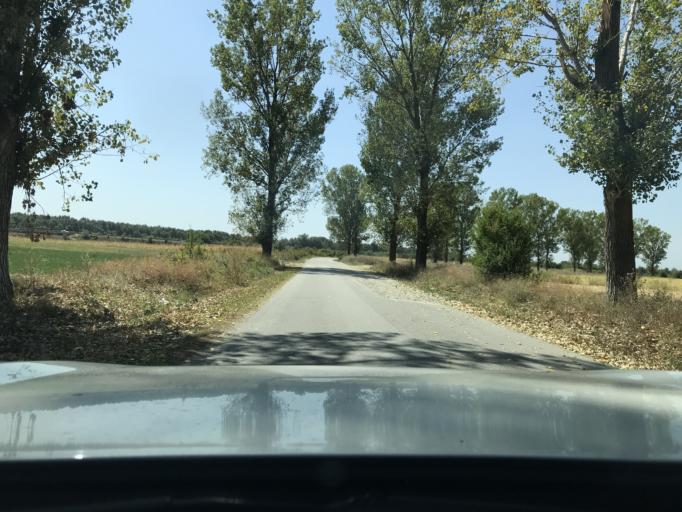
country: RO
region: Olt
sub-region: Comuna Falcoiu
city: Falcoiu
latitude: 44.2362
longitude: 24.3409
